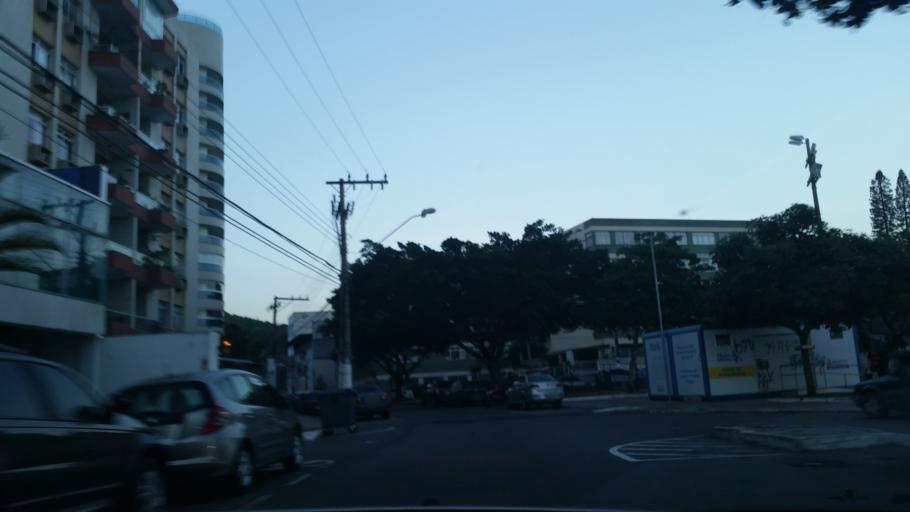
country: BR
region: Espirito Santo
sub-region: Vila Velha
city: Vila Velha
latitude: -20.3296
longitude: -40.2736
